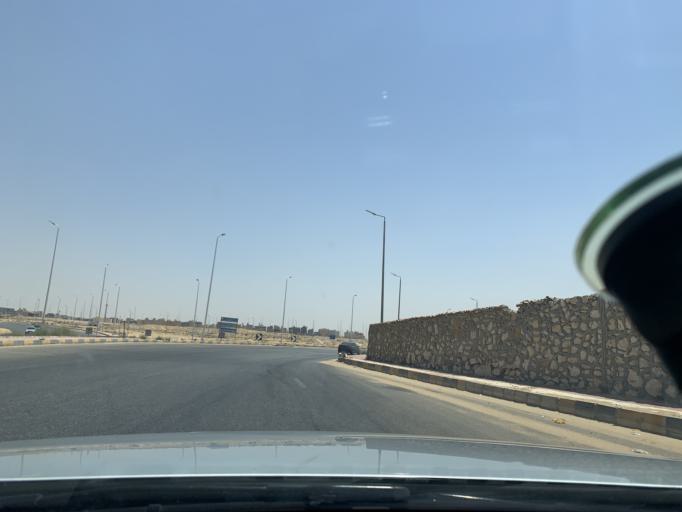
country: EG
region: Muhafazat al Qahirah
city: Halwan
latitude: 29.9765
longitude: 31.4700
